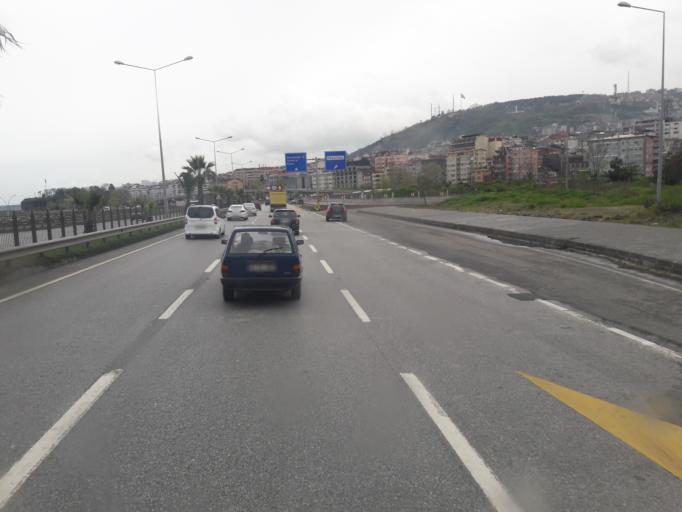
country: TR
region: Trabzon
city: Trabzon
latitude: 41.0112
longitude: 39.7235
